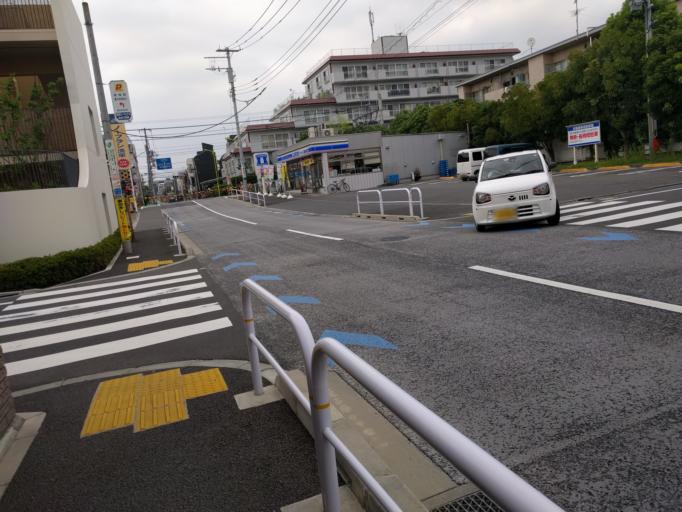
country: JP
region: Tokyo
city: Tokyo
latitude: 35.6056
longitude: 139.6577
